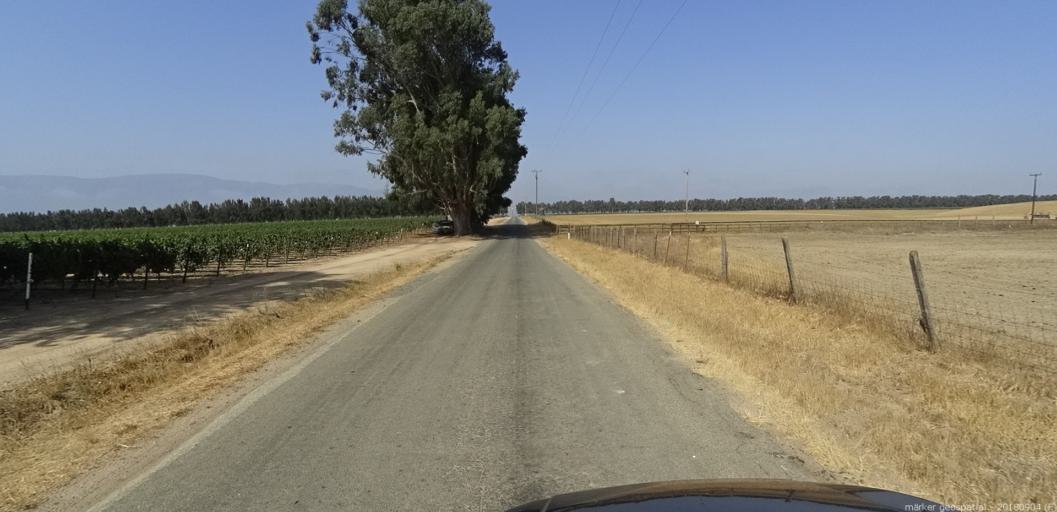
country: US
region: California
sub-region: Monterey County
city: Soledad
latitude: 36.4816
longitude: -121.3522
